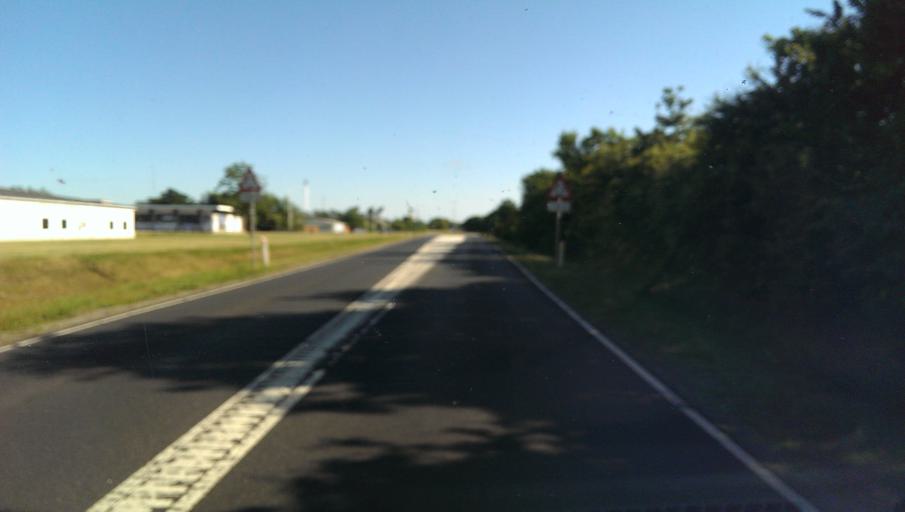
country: DK
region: South Denmark
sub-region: Esbjerg Kommune
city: Esbjerg
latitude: 55.5121
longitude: 8.4059
